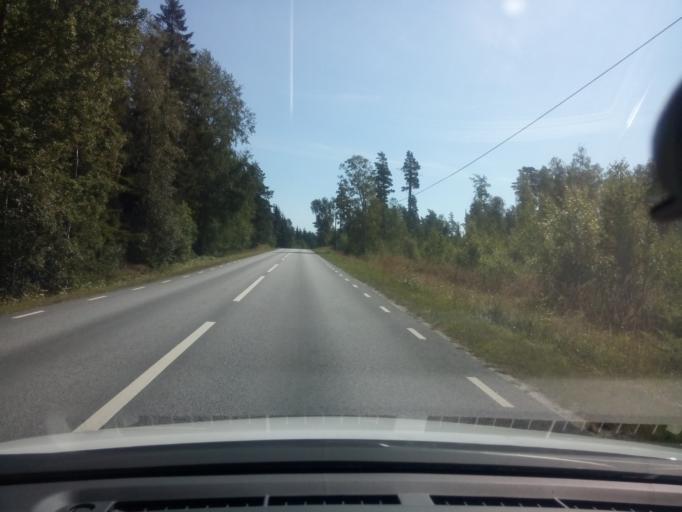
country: SE
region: Soedermanland
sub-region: Oxelosunds Kommun
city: Oxelosund
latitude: 58.7411
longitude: 17.1735
